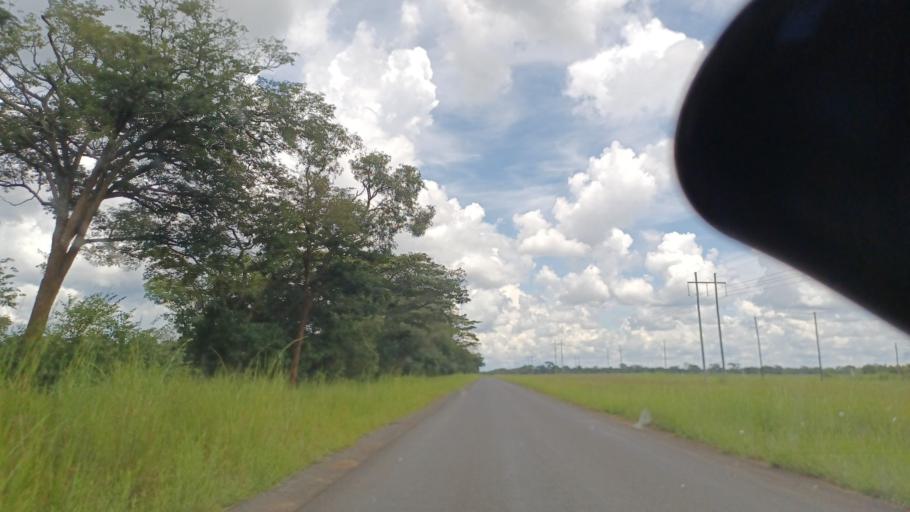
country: ZM
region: North-Western
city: Solwezi
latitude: -12.4520
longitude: 26.2053
